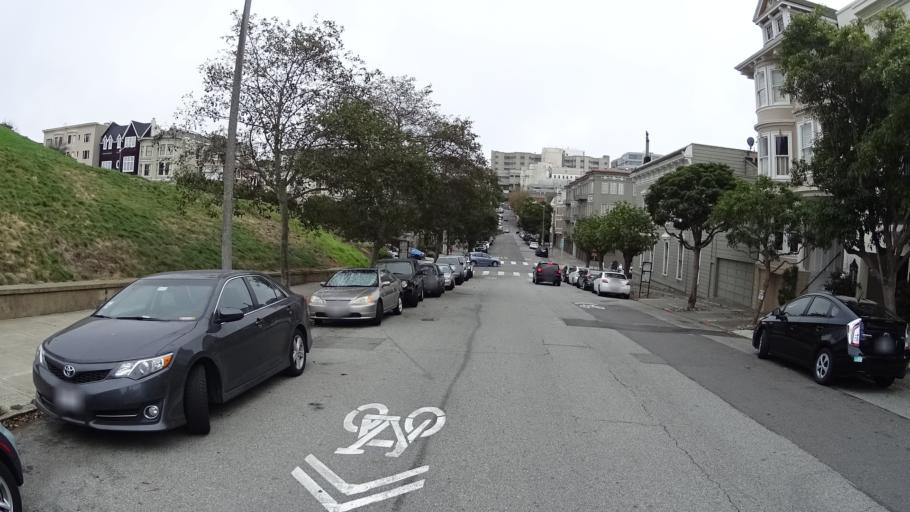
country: US
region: California
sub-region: San Francisco County
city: San Francisco
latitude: 37.7904
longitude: -122.4365
